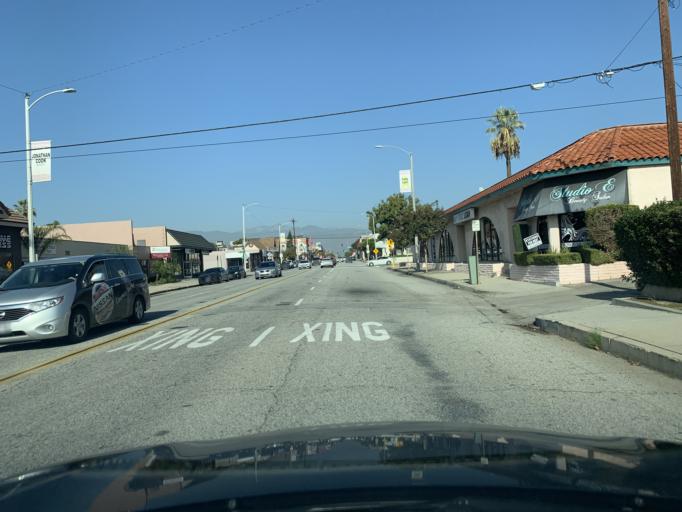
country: US
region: California
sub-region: Los Angeles County
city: Covina
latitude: 34.0843
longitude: -117.8901
